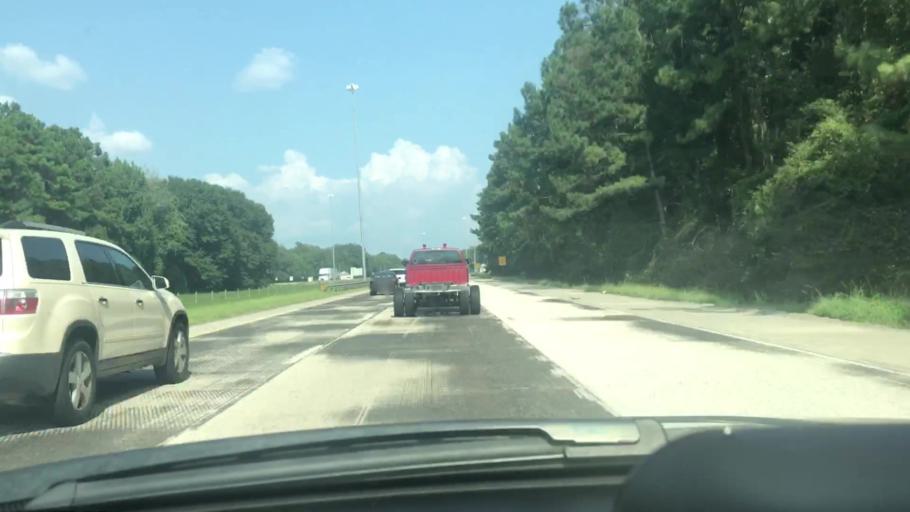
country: US
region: Louisiana
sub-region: Livingston Parish
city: Albany
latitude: 30.4793
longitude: -90.5266
